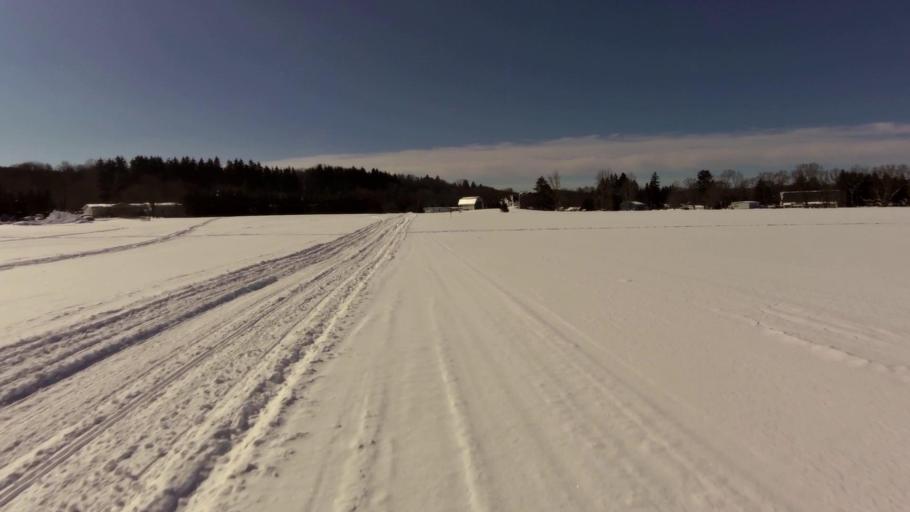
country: US
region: New York
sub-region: Cattaraugus County
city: Franklinville
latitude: 42.3458
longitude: -78.4481
